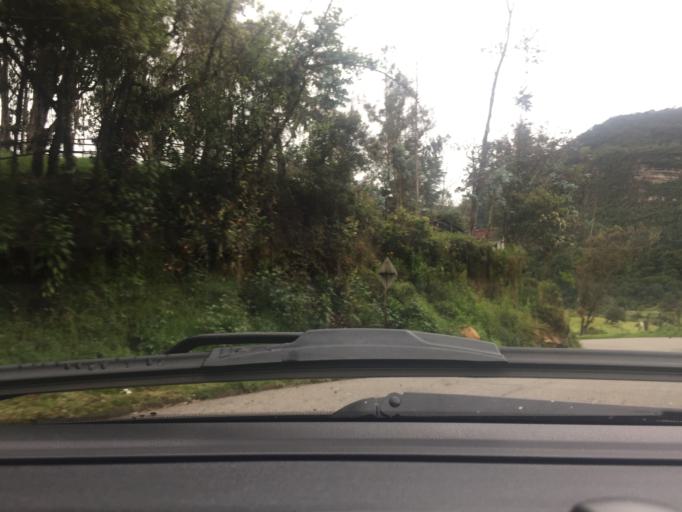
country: CO
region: Cundinamarca
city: Junin
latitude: 4.8195
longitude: -73.7487
